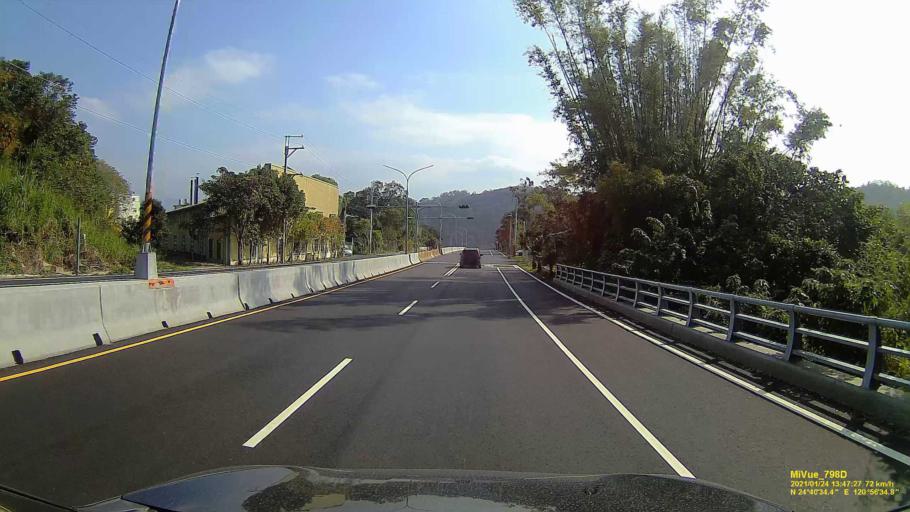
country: TW
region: Taiwan
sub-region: Hsinchu
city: Hsinchu
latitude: 24.6759
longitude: 120.9432
